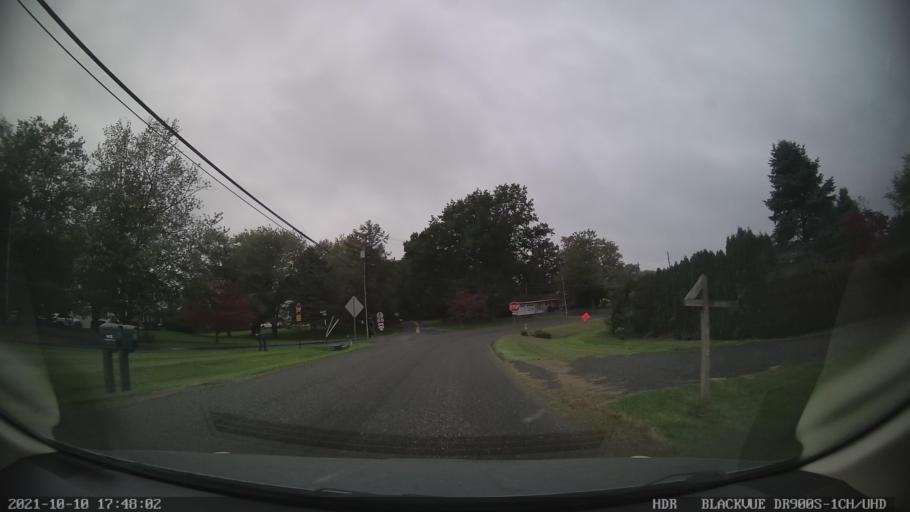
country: US
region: Pennsylvania
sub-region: Lehigh County
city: Breinigsville
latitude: 40.5762
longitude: -75.6919
